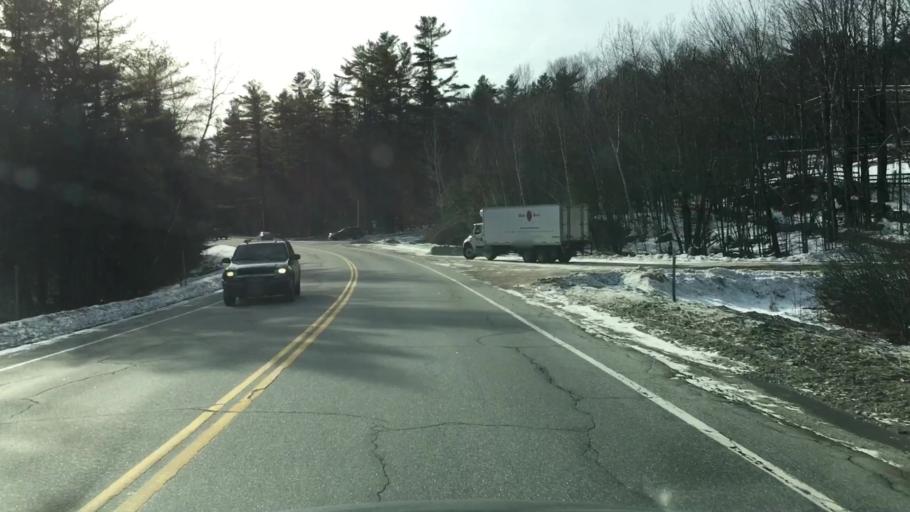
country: US
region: New Hampshire
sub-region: Sullivan County
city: Sunapee
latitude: 43.4195
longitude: -72.0812
